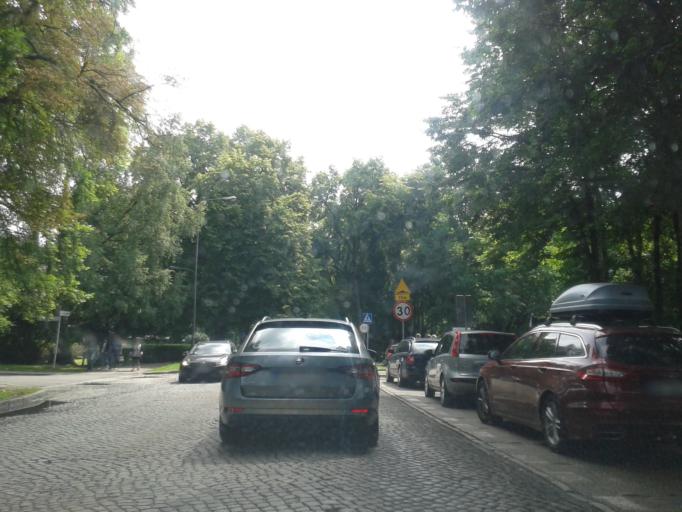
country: PL
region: West Pomeranian Voivodeship
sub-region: Swinoujscie
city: Swinoujscie
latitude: 53.9164
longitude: 14.2309
